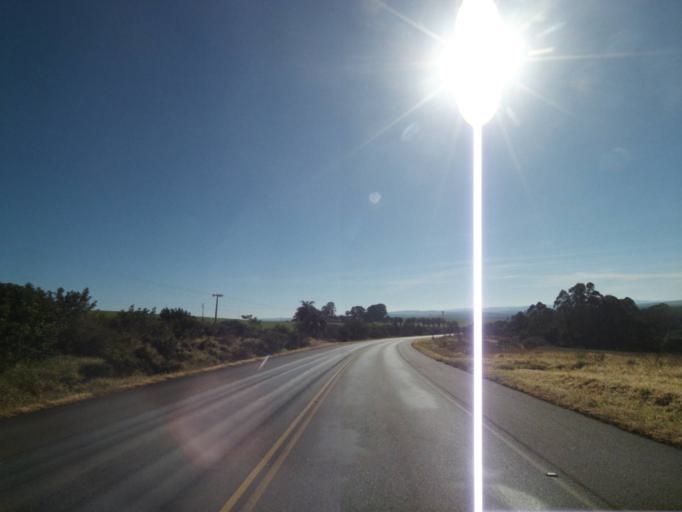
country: BR
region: Parana
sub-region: Tibagi
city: Tibagi
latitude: -24.4958
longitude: -50.4448
